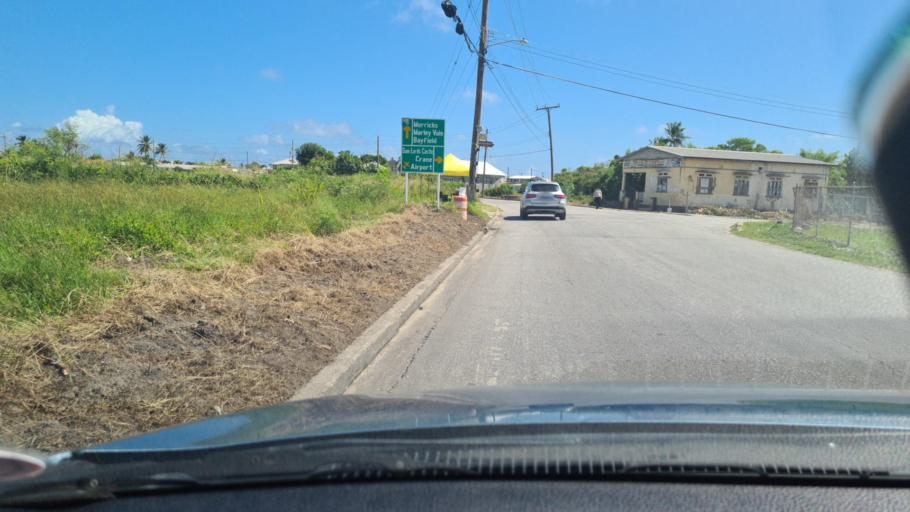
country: BB
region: Saint Philip
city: Crane
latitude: 13.1311
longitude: -59.4411
